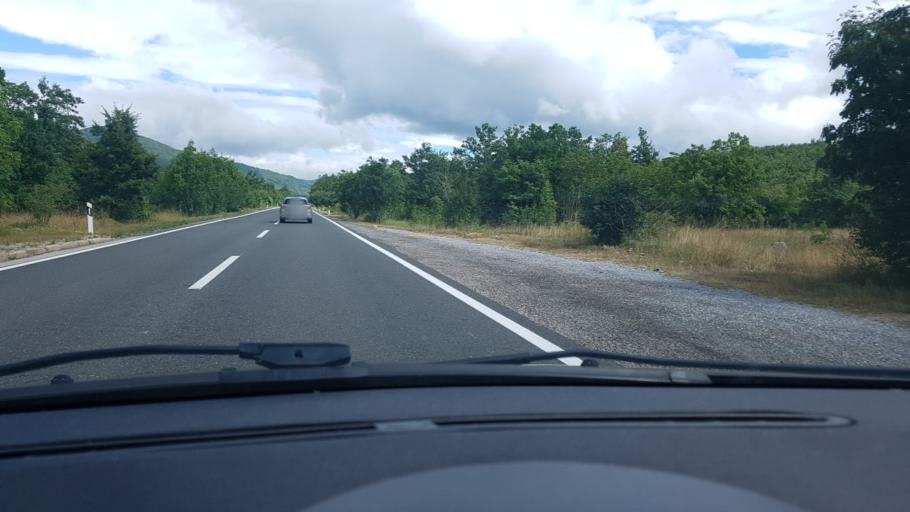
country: HR
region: Zadarska
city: Gracac
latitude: 44.4575
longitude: 15.8187
